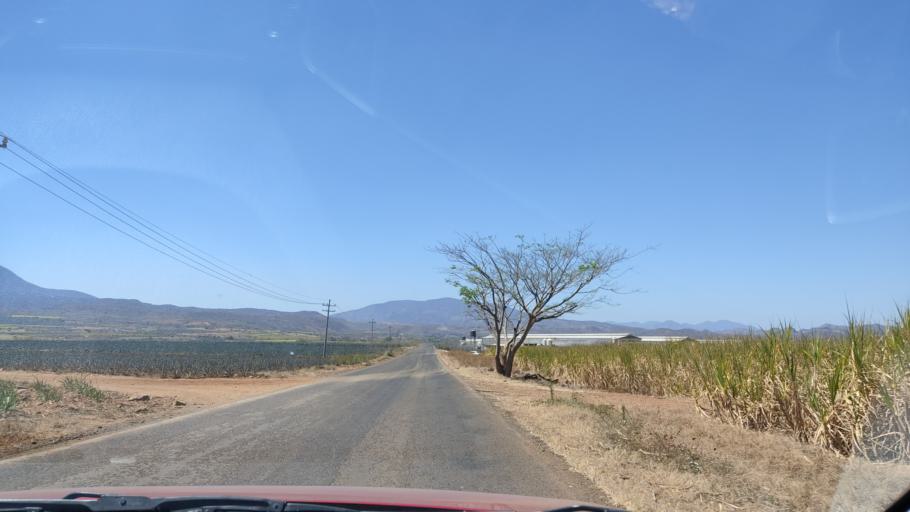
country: MX
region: Nayarit
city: Santa Maria del Oro
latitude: 21.4361
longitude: -104.6201
